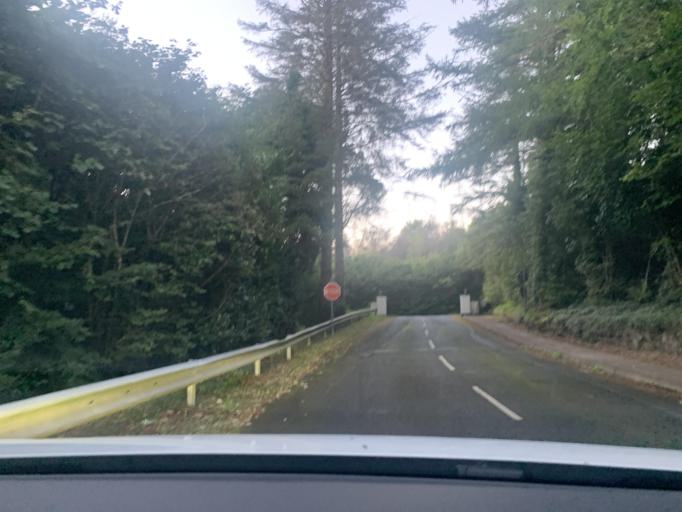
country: IE
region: Connaught
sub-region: Sligo
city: Sligo
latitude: 54.2620
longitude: -8.3874
